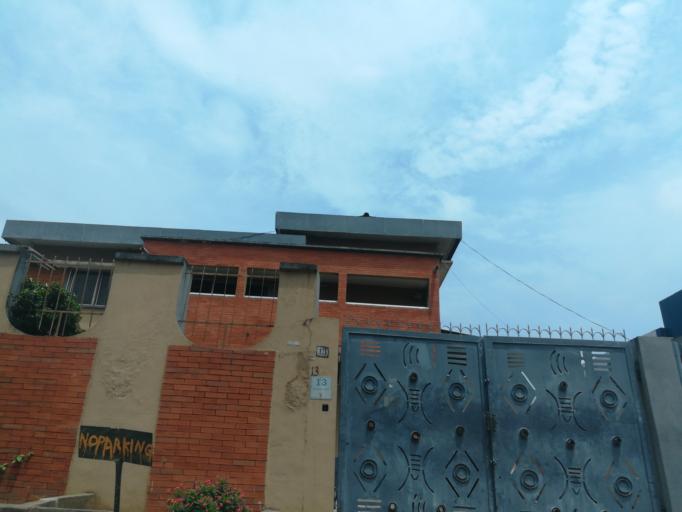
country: NG
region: Lagos
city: Ojota
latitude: 6.5906
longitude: 3.3628
